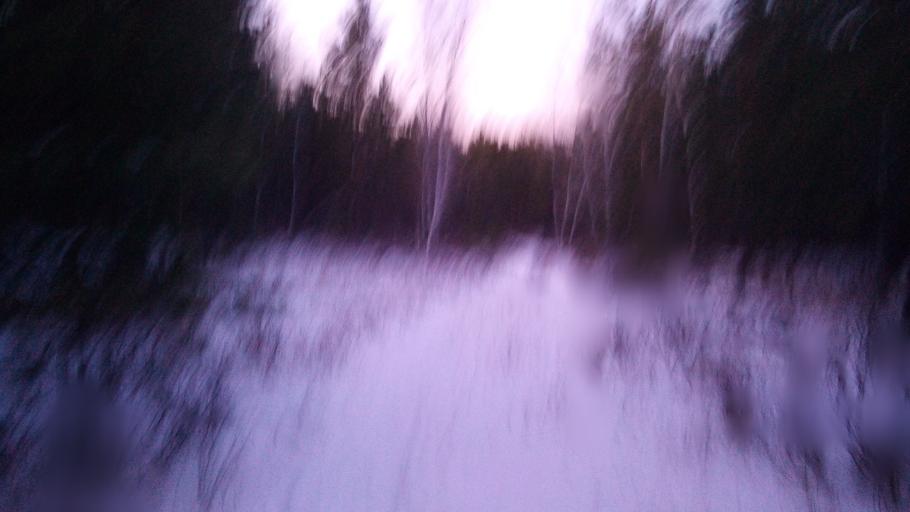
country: RU
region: Chelyabinsk
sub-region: Gorod Chelyabinsk
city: Chelyabinsk
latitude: 55.1626
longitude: 61.3330
